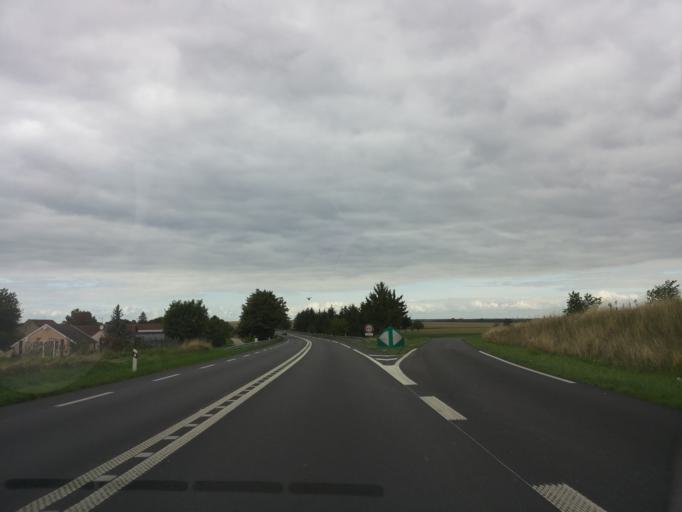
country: FR
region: Champagne-Ardenne
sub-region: Departement de la Marne
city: Verzy
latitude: 49.1357
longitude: 4.2312
